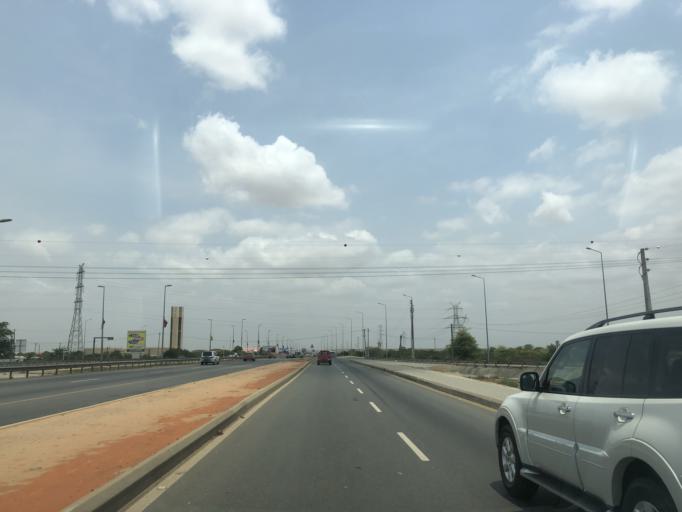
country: AO
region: Luanda
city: Luanda
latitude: -8.9737
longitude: 13.2552
